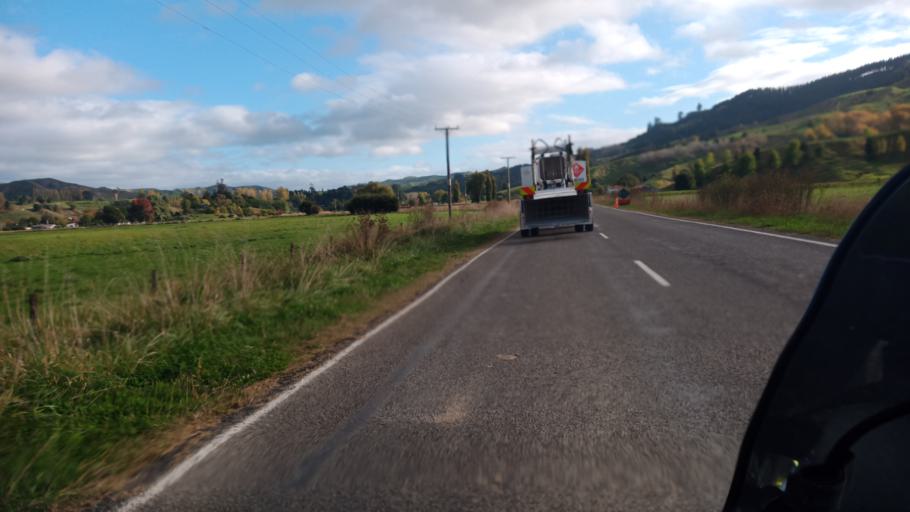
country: NZ
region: Gisborne
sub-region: Gisborne District
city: Gisborne
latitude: -38.5913
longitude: 177.7968
